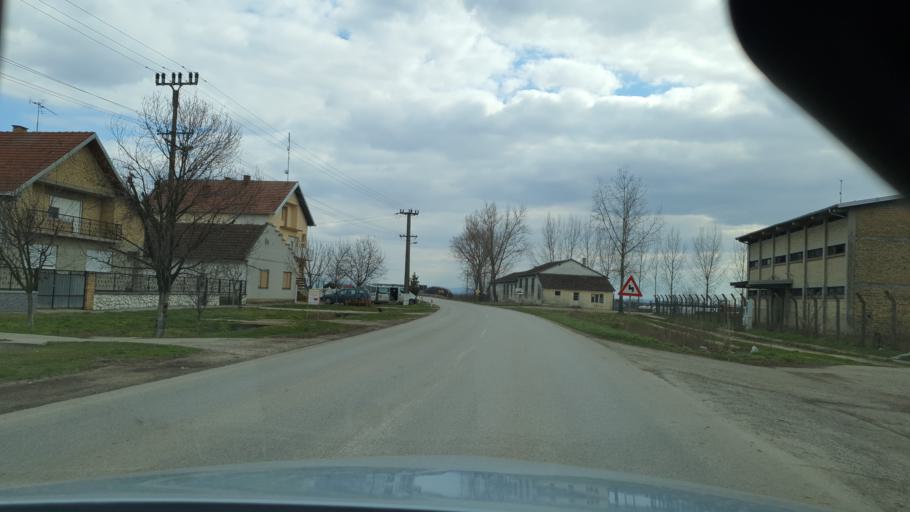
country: RS
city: Obrovac
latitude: 45.4141
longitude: 19.4037
